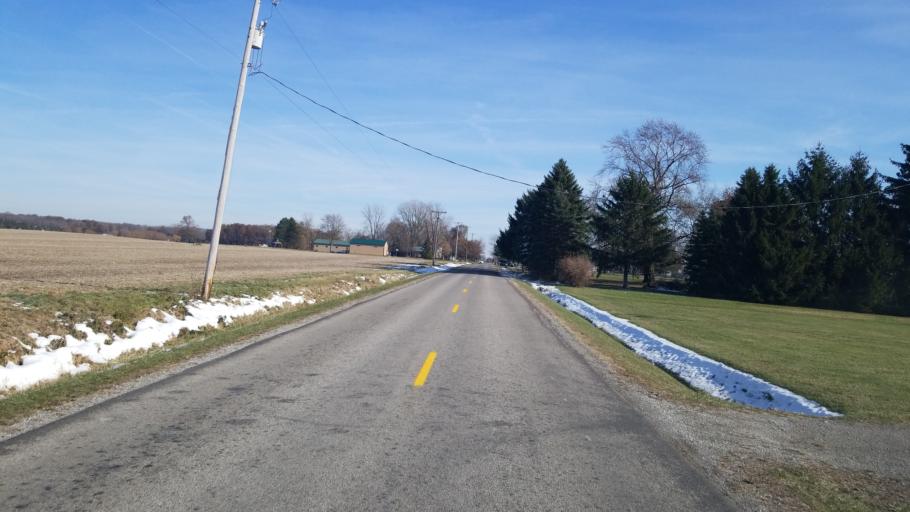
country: US
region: Ohio
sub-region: Huron County
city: Norwalk
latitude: 41.2037
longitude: -82.5062
